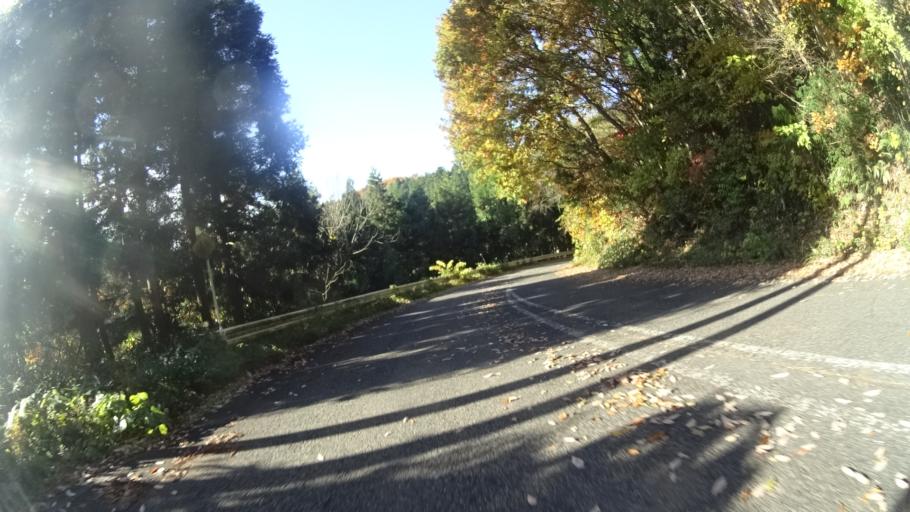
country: JP
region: Niigata
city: Yoshida-kasugacho
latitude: 37.6561
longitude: 138.8130
